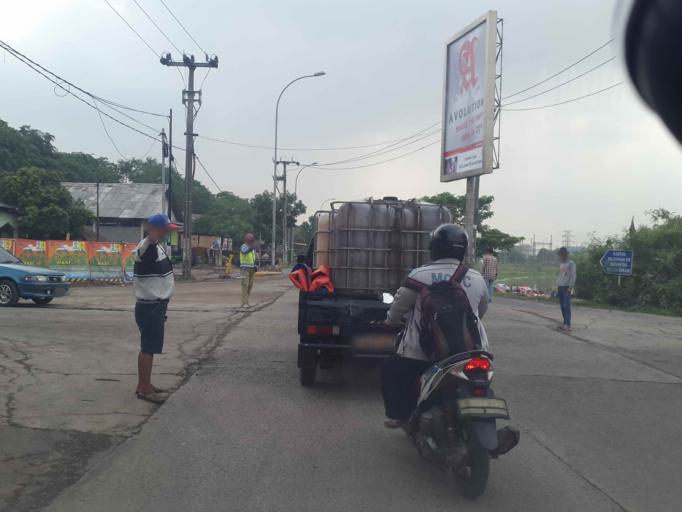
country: ID
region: West Java
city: Cikarang
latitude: -6.2846
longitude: 107.1130
